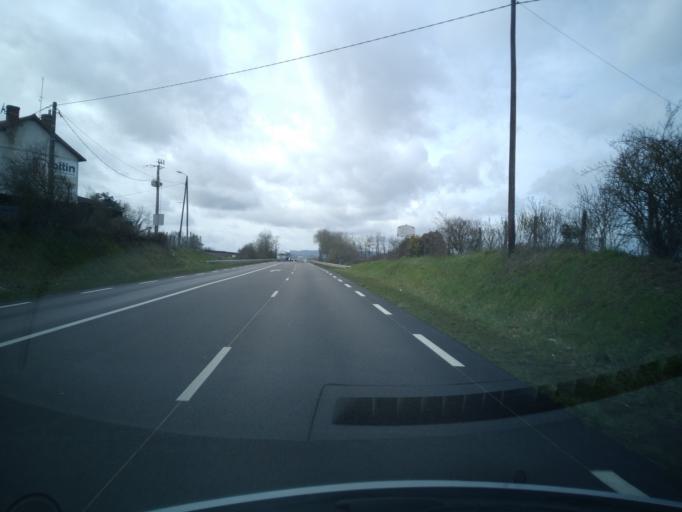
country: FR
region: Bourgogne
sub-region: Departement de Saone-et-Loire
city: Montchanin
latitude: 46.7586
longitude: 4.4691
